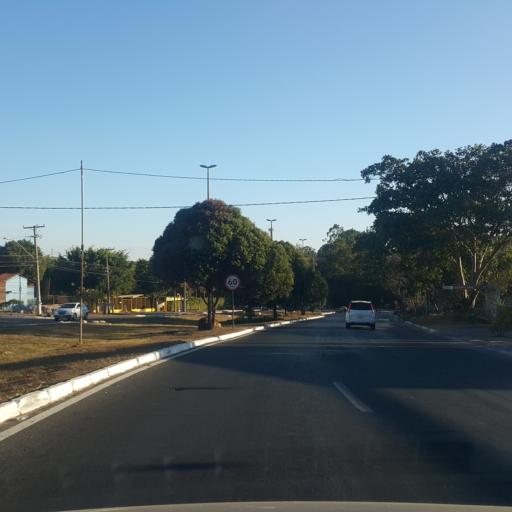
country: BR
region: Federal District
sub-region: Brasilia
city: Brasilia
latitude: -15.8555
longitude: -47.9756
